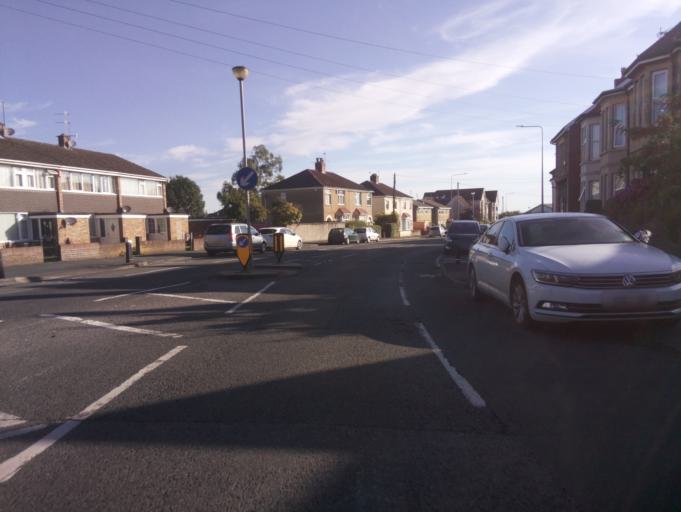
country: GB
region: England
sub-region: South Gloucestershire
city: Mangotsfield
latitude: 51.4716
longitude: -2.5097
